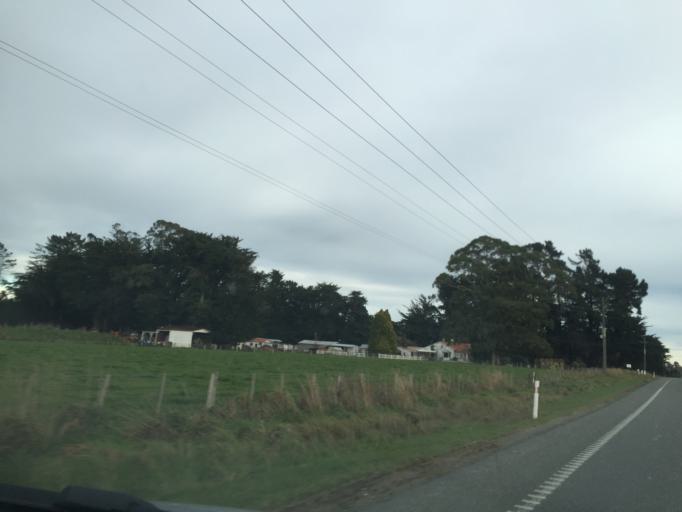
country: NZ
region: Southland
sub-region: Gore District
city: Gore
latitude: -46.3097
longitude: 168.7662
